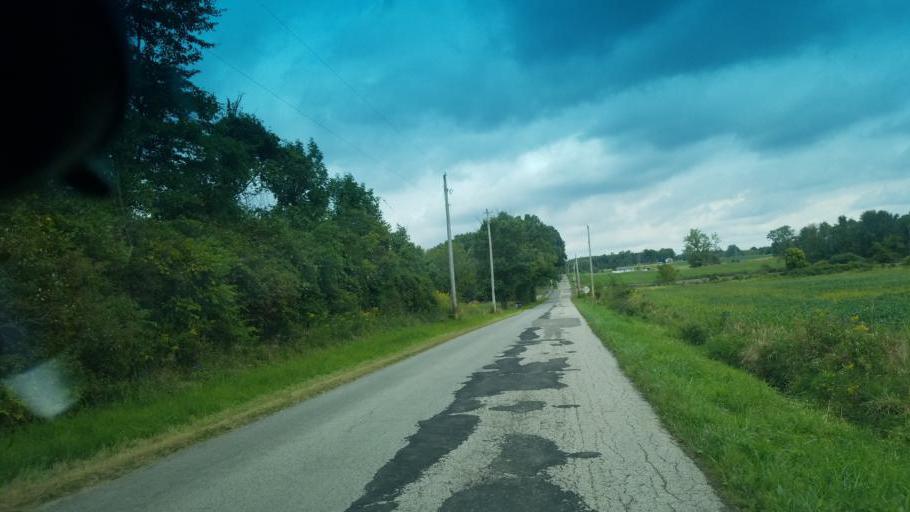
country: US
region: Ohio
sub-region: Richland County
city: Ontario
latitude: 40.8064
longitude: -82.5709
